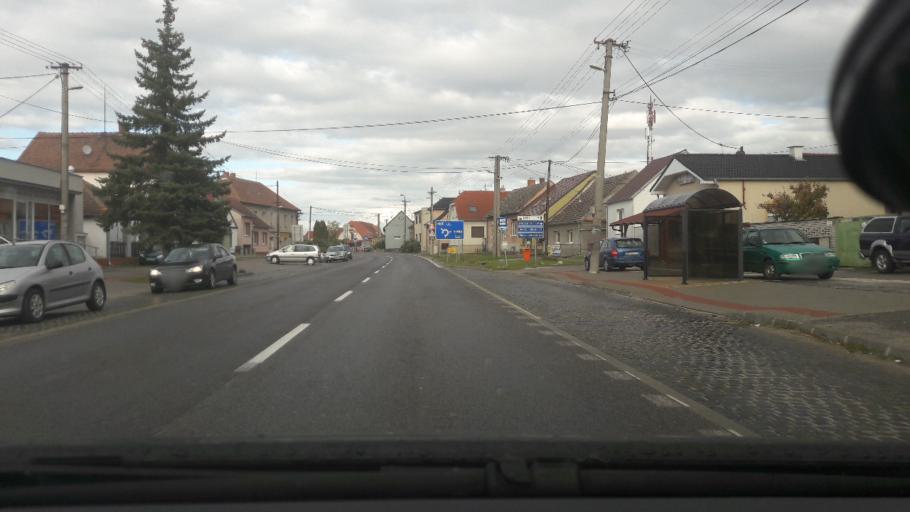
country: CZ
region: South Moravian
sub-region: Okres Breclav
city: Lanzhot
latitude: 48.6570
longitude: 17.0191
